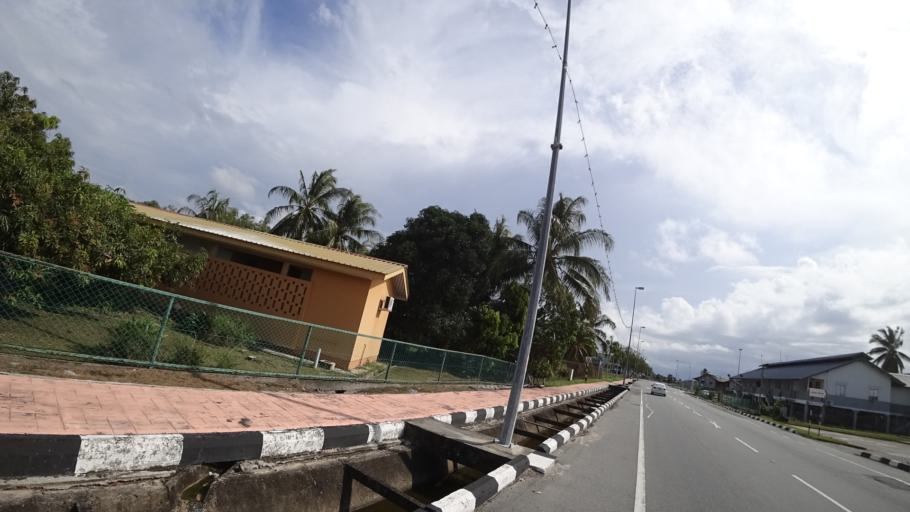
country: BN
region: Tutong
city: Tutong
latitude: 4.8095
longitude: 114.6605
